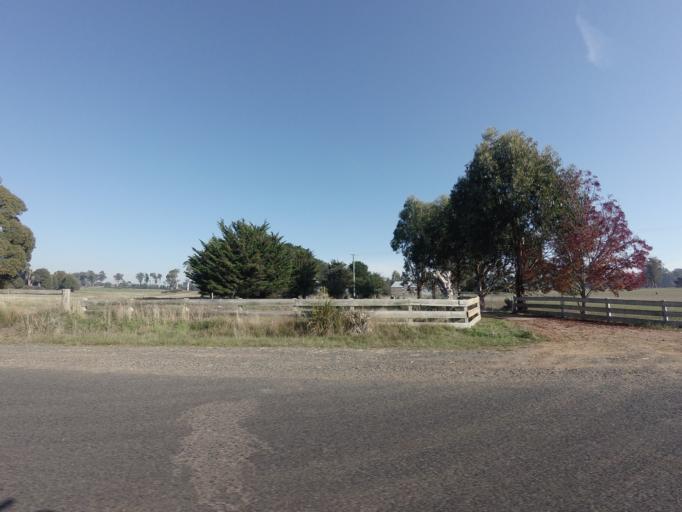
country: AU
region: Tasmania
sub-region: Northern Midlands
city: Longford
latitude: -41.5413
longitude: 146.9918
